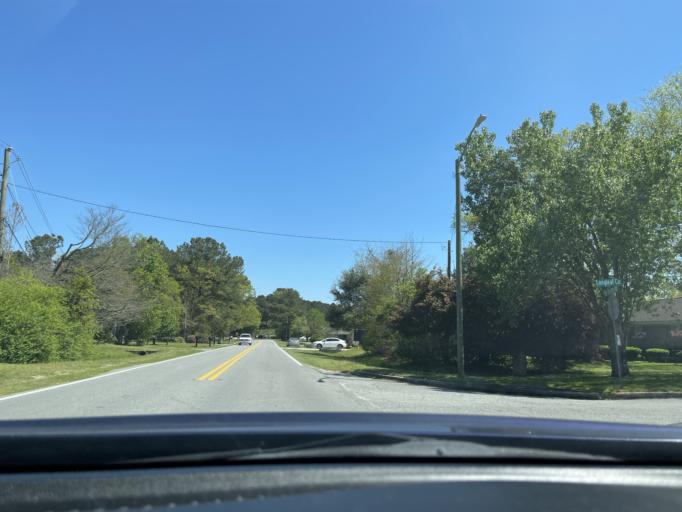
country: US
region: Georgia
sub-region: Chatham County
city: Pooler
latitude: 32.0906
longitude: -81.2495
